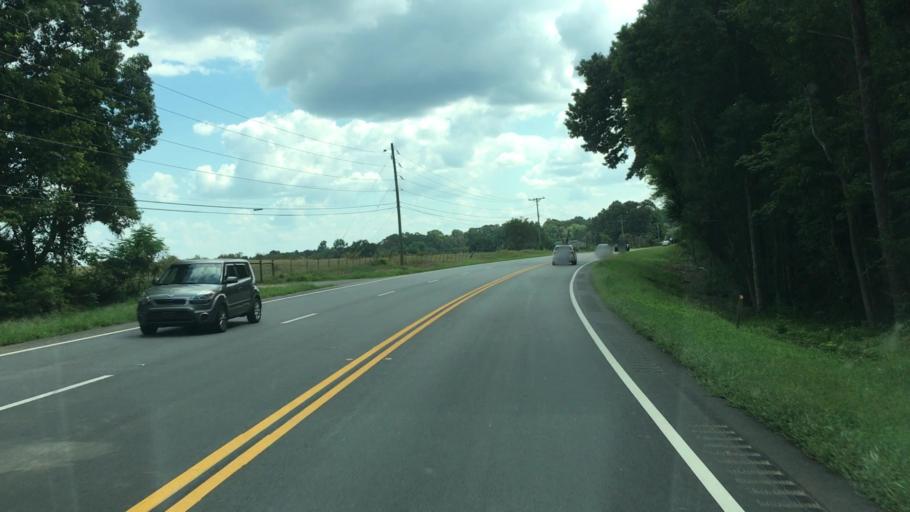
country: US
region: Georgia
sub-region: Putnam County
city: Jefferson
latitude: 33.4240
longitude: -83.3701
